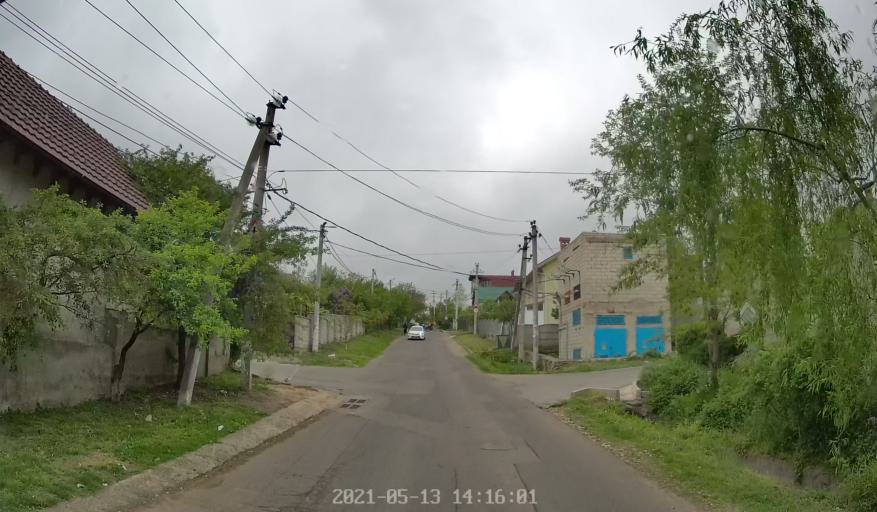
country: MD
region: Chisinau
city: Stauceni
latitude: 47.0961
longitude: 28.8665
